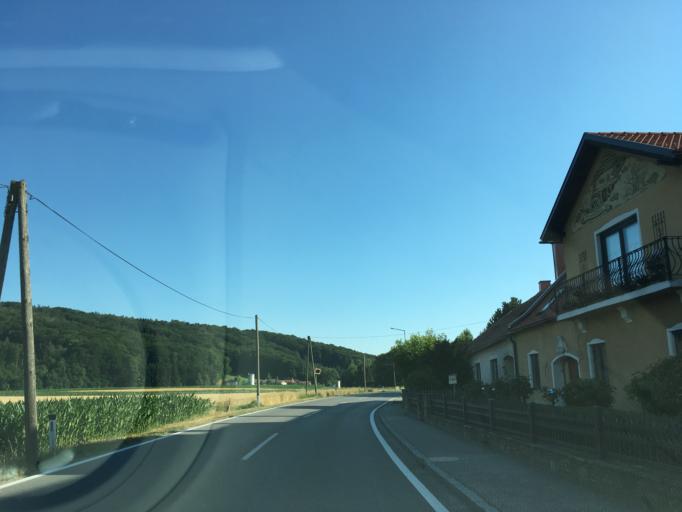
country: AT
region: Lower Austria
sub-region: Politischer Bezirk Sankt Polten
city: Boheimkirchen
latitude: 48.1796
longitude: 15.7586
